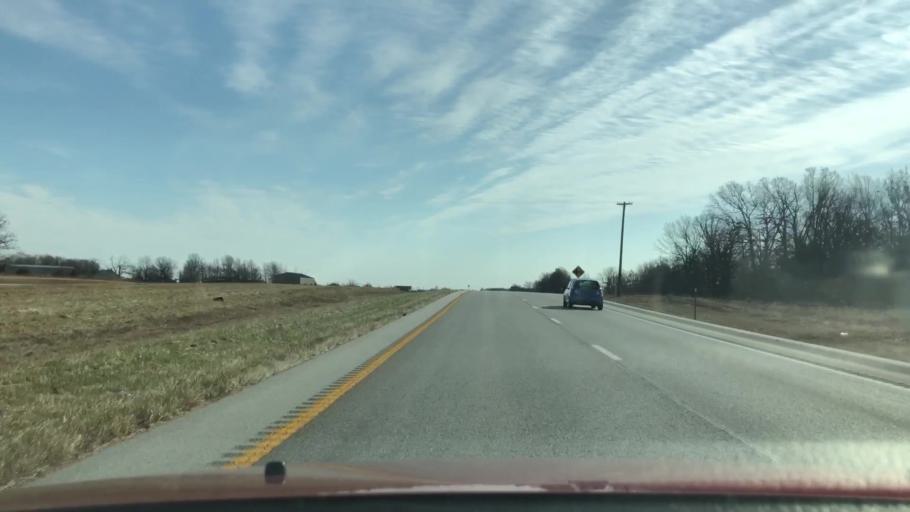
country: US
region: Missouri
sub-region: Webster County
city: Seymour
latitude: 37.1645
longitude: -92.8004
